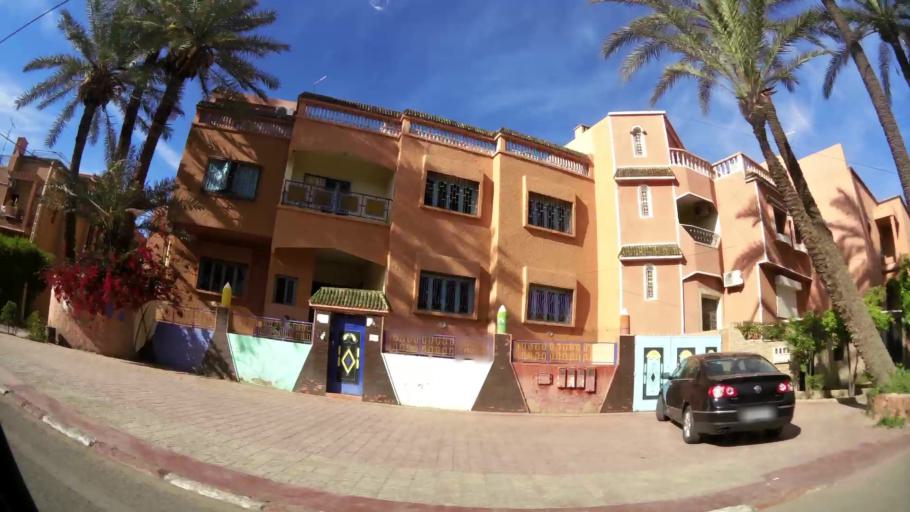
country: MA
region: Marrakech-Tensift-Al Haouz
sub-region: Marrakech
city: Marrakesh
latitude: 31.6569
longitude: -8.0142
